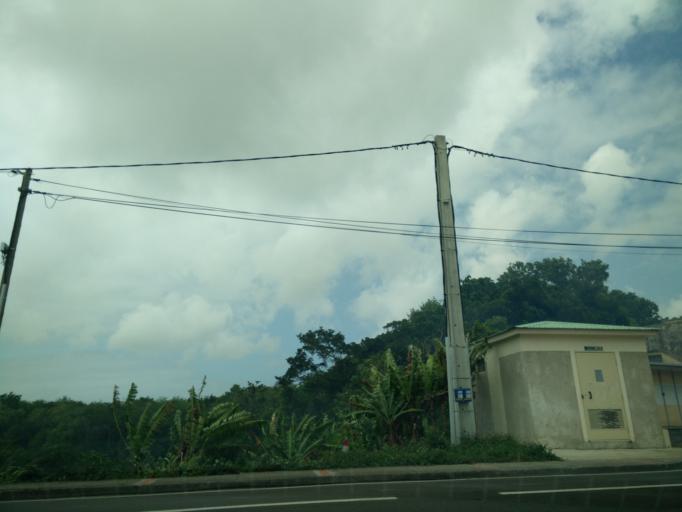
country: GP
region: Guadeloupe
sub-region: Guadeloupe
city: Grand-Bourg
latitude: 15.9076
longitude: -61.2764
